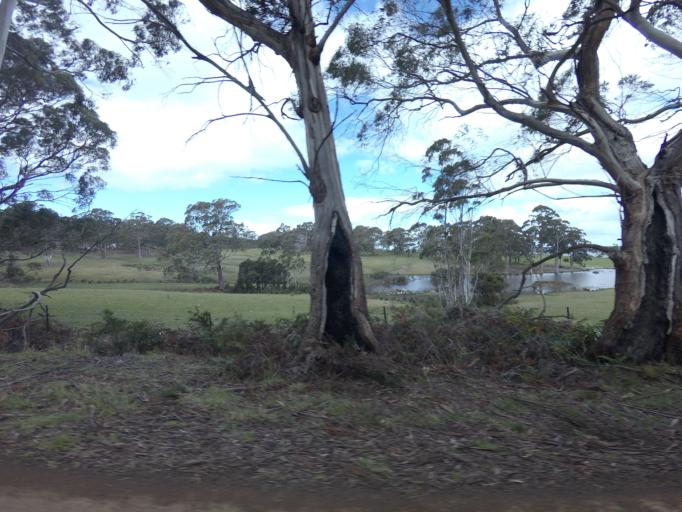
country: AU
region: Tasmania
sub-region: Huon Valley
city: Geeveston
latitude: -43.4259
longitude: 146.9981
